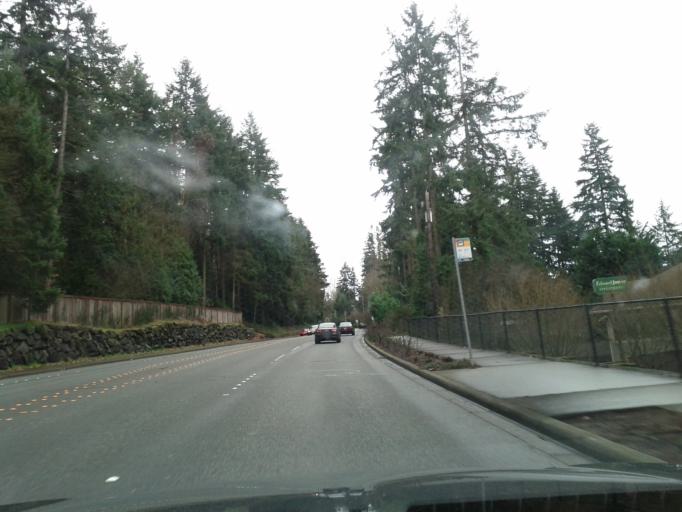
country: US
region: Washington
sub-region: King County
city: Eastgate
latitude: 47.5751
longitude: -122.1403
